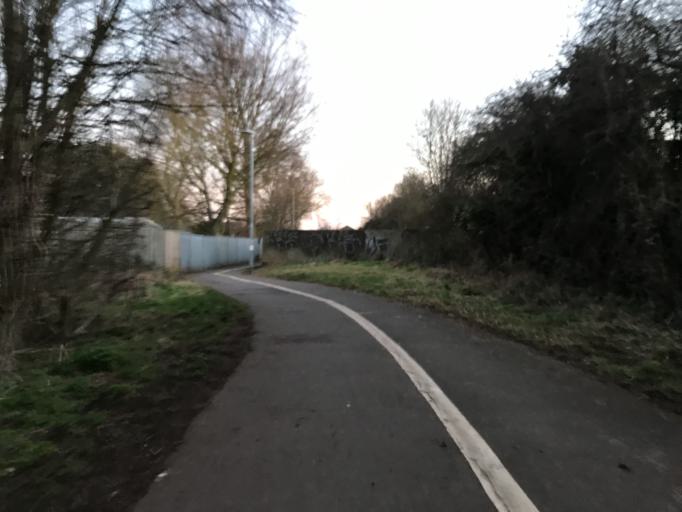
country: GB
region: England
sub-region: Lincolnshire
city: Holton le Clay
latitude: 53.5256
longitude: -0.0644
